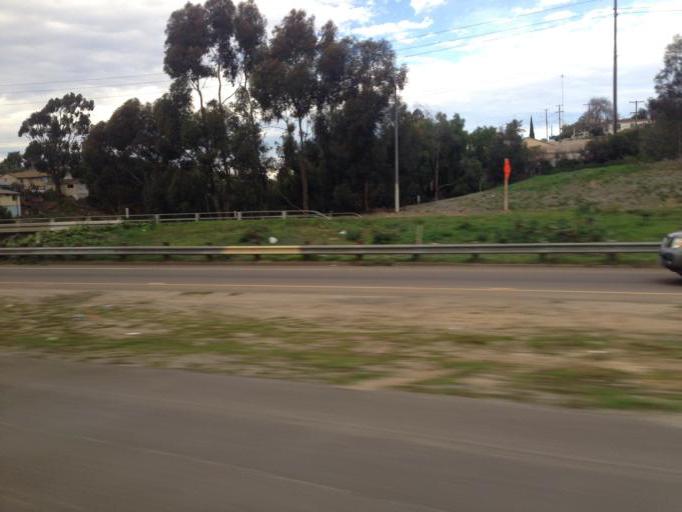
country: US
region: California
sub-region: San Diego County
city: Chula Vista
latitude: 32.6623
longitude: -117.0778
